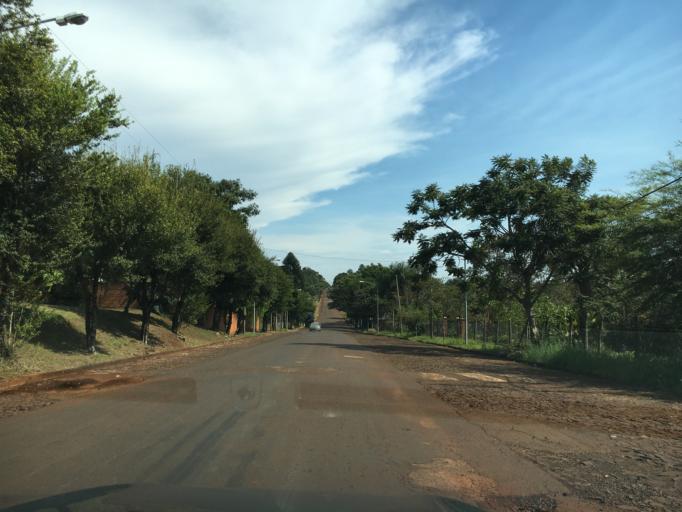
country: AR
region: Misiones
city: Puerto Rico
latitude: -26.8064
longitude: -55.0152
